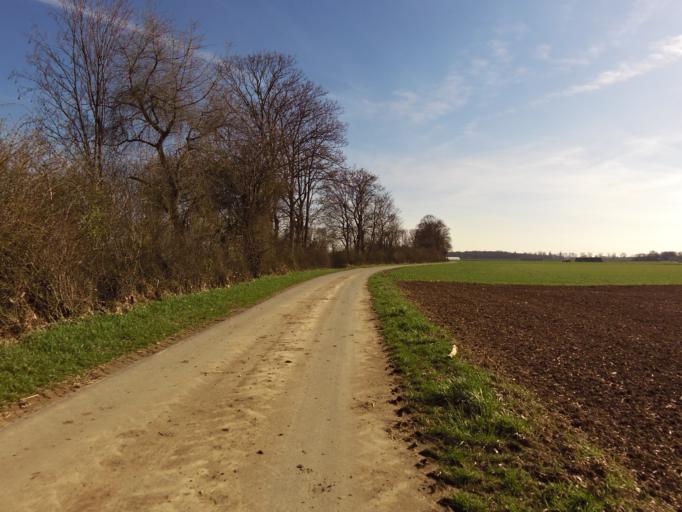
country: DE
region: Hesse
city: Biebesheim
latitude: 49.7880
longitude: 8.4361
